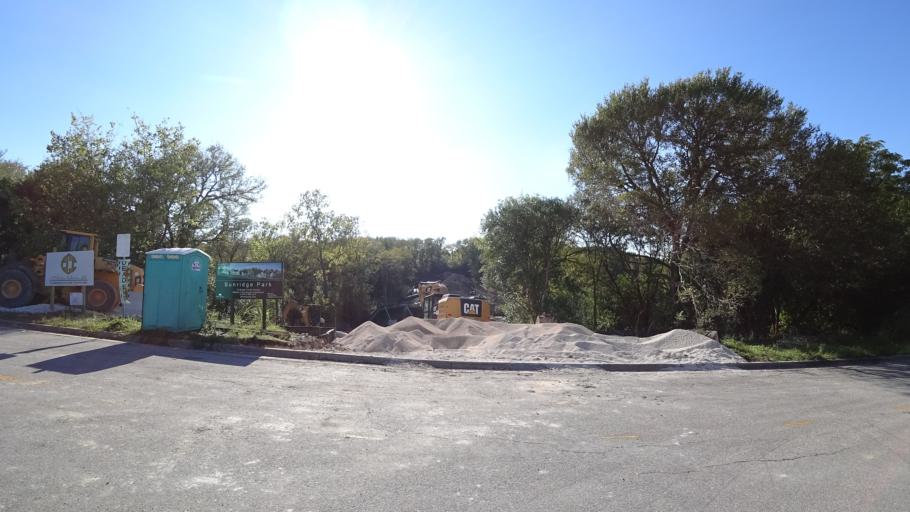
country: US
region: Texas
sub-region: Travis County
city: Austin
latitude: 30.2182
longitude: -97.7267
